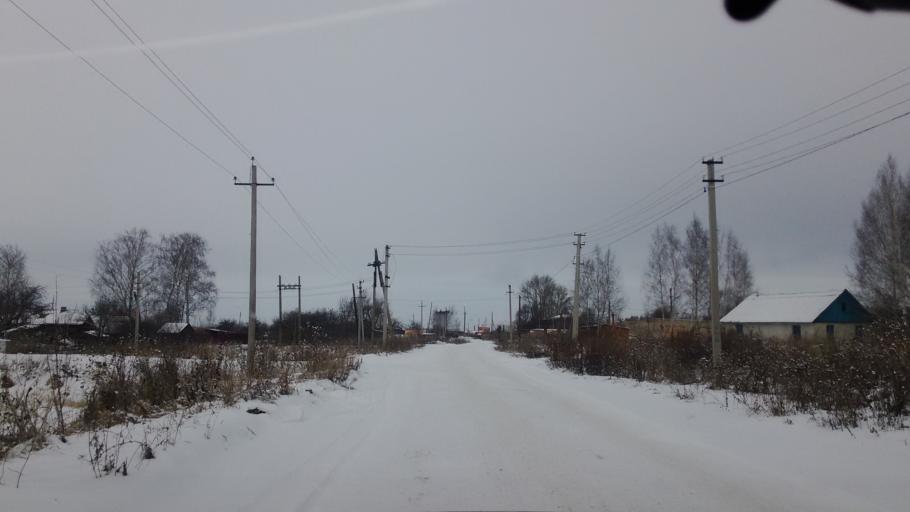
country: RU
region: Tula
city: Bogoroditsk
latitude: 53.7650
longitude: 38.1017
